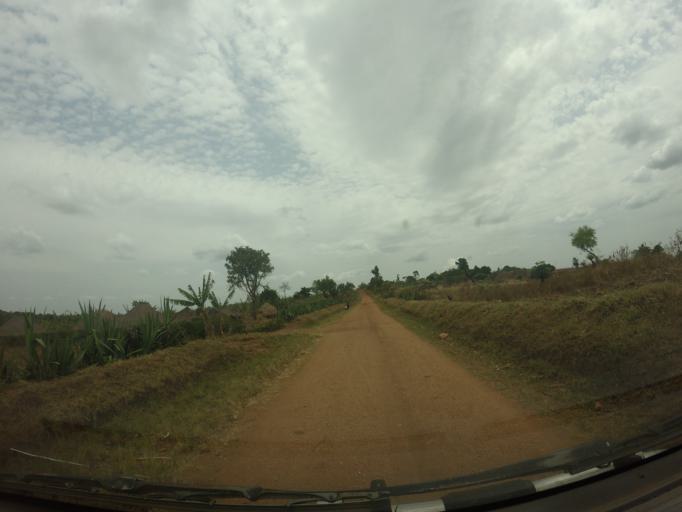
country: UG
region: Northern Region
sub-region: Arua District
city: Arua
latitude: 2.8228
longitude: 30.9035
